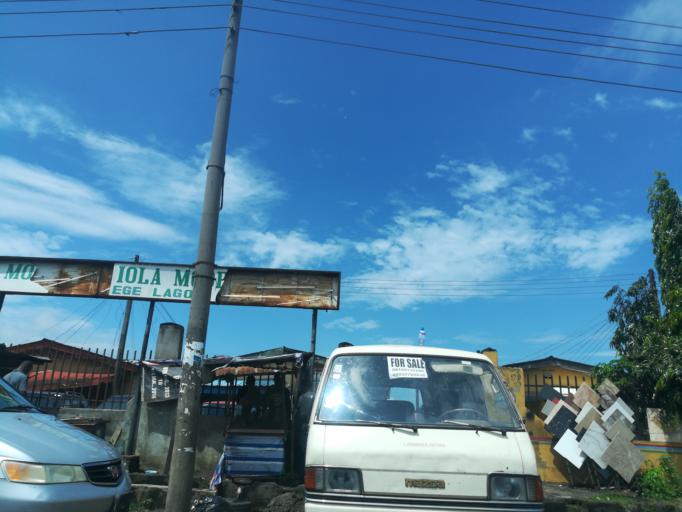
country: NG
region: Lagos
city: Agege
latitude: 6.6210
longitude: 3.3295
